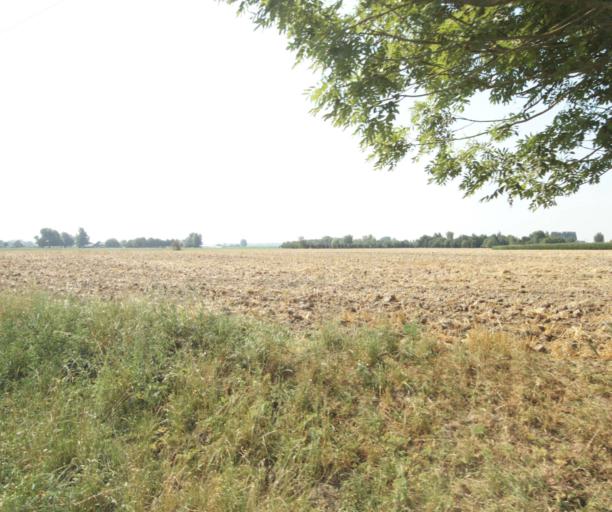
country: FR
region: Nord-Pas-de-Calais
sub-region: Departement du Nord
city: Quesnoy-sur-Deule
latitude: 50.7079
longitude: 2.9821
